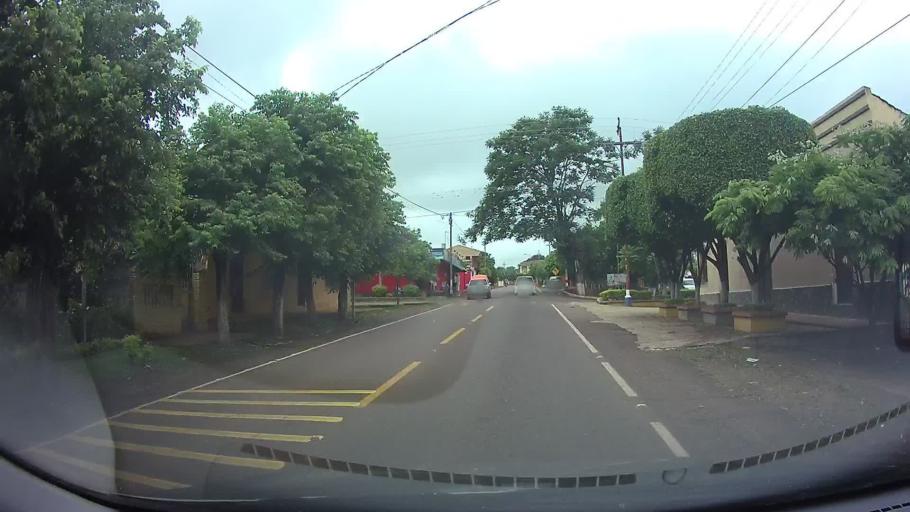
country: PY
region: Paraguari
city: Acahay
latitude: -25.9129
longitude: -57.1150
